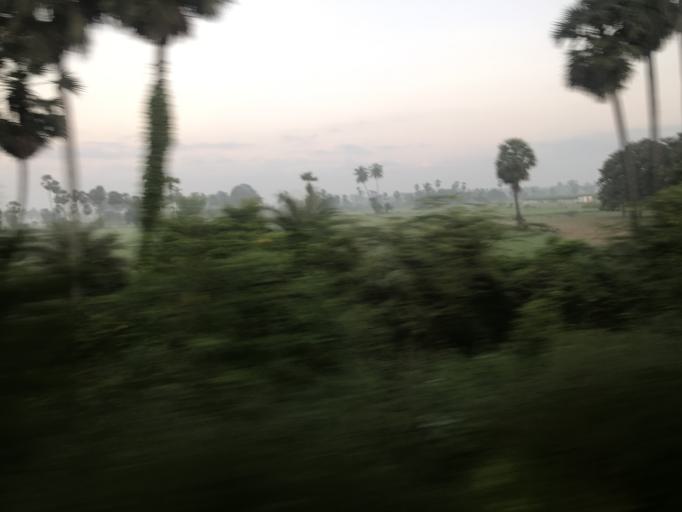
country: IN
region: Andhra Pradesh
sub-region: Guntur
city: Ponnur
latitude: 16.1091
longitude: 80.5761
